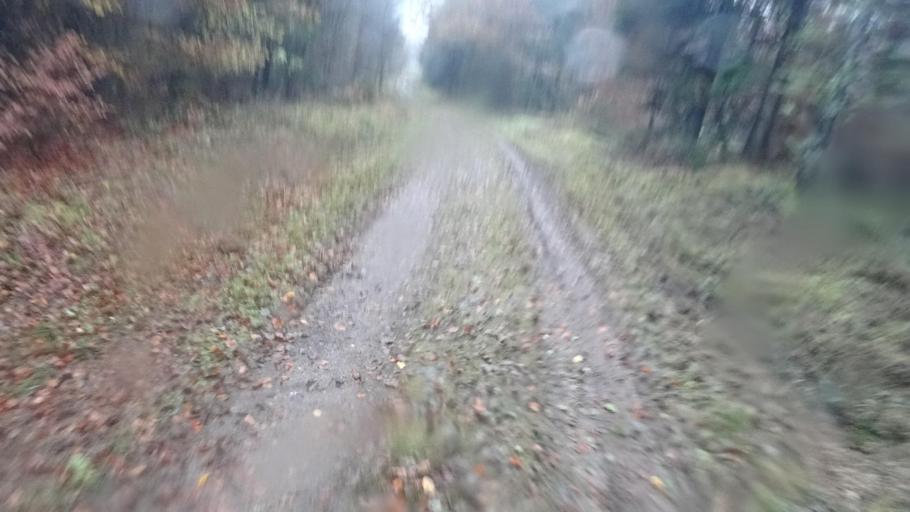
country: DE
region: Rheinland-Pfalz
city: Maisborn
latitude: 50.0898
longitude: 7.5780
